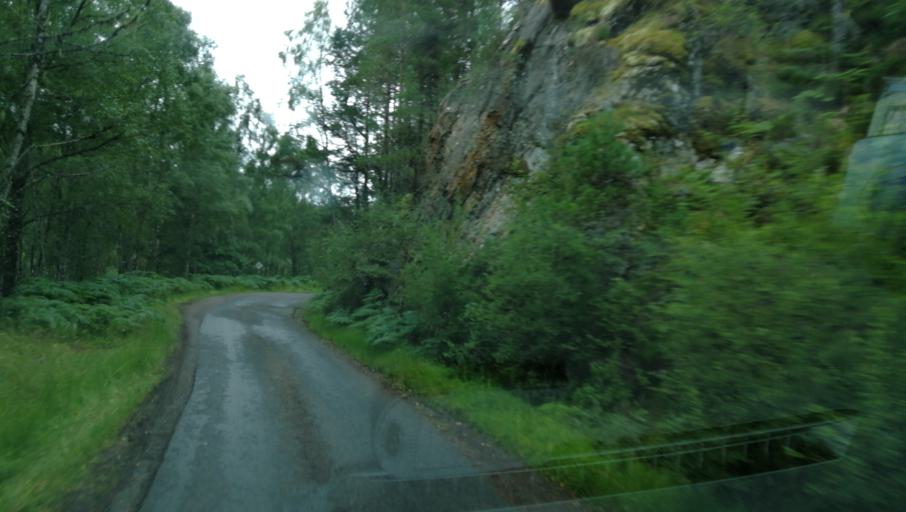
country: GB
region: Scotland
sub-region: Highland
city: Spean Bridge
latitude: 57.3077
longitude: -4.8674
